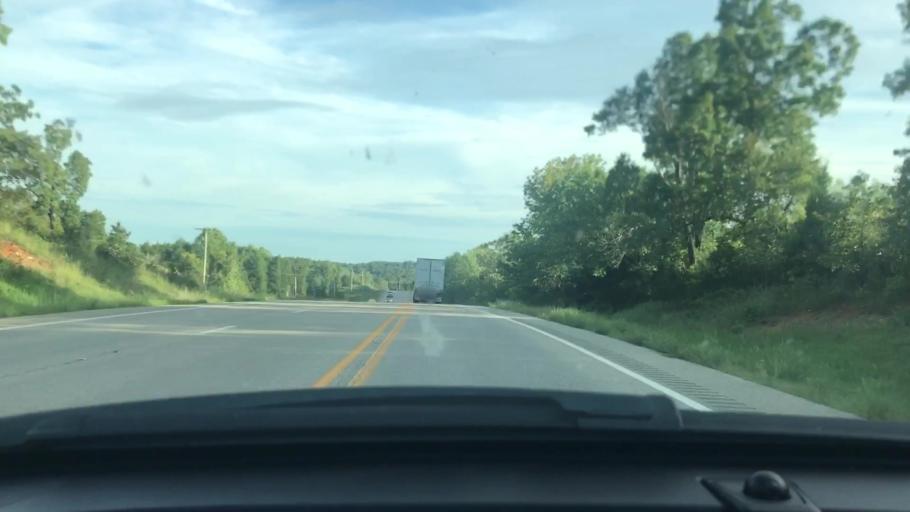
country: US
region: Arkansas
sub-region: Lawrence County
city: Hoxie
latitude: 36.1482
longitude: -91.1601
